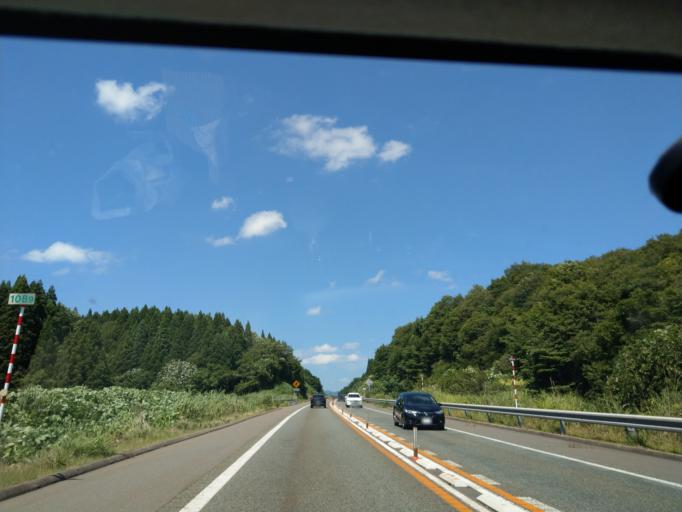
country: JP
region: Akita
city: Akita
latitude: 39.6791
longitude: 140.1856
